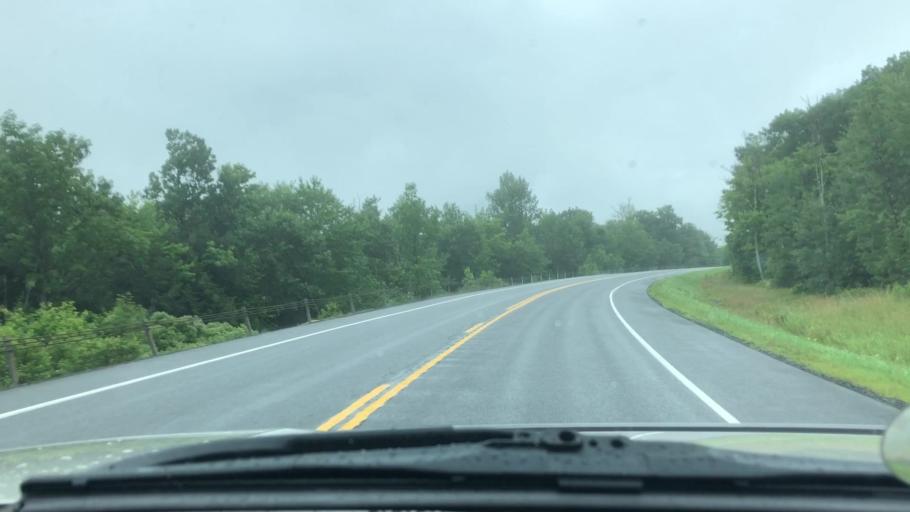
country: US
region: New York
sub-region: Greene County
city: Cairo
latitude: 42.3306
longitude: -74.1665
